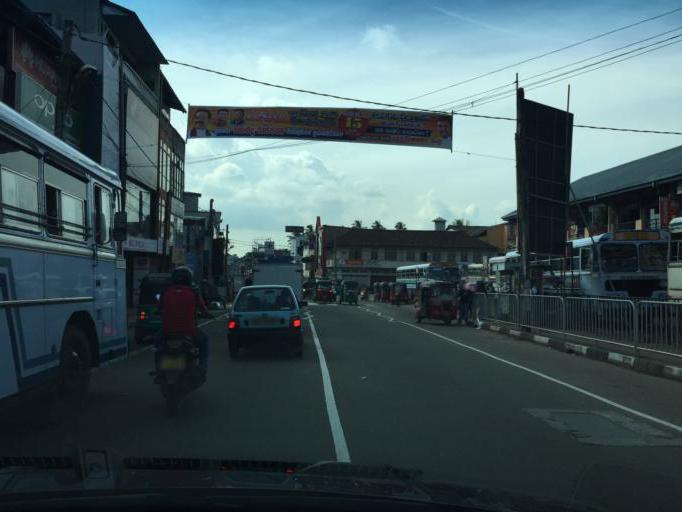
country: LK
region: Western
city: Horana South
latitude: 6.7166
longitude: 80.0636
